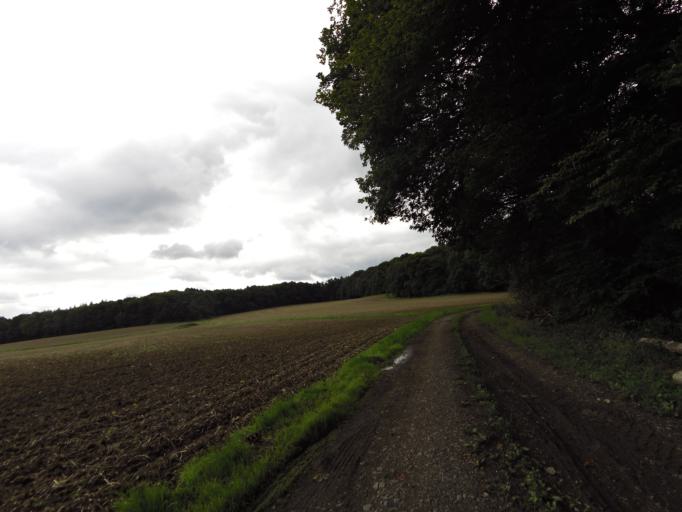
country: DE
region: Rheinland-Pfalz
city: Dernau
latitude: 50.5513
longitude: 7.0778
